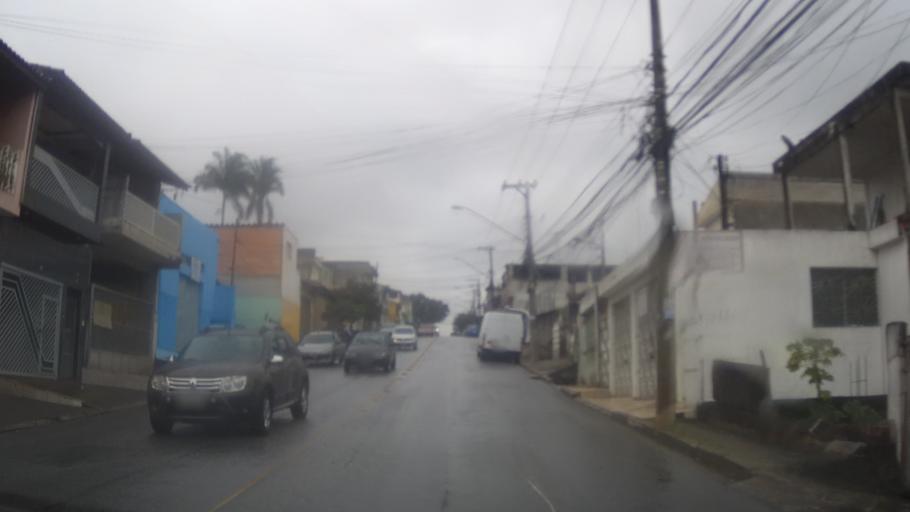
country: BR
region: Sao Paulo
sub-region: Guarulhos
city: Guarulhos
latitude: -23.4389
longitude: -46.5268
